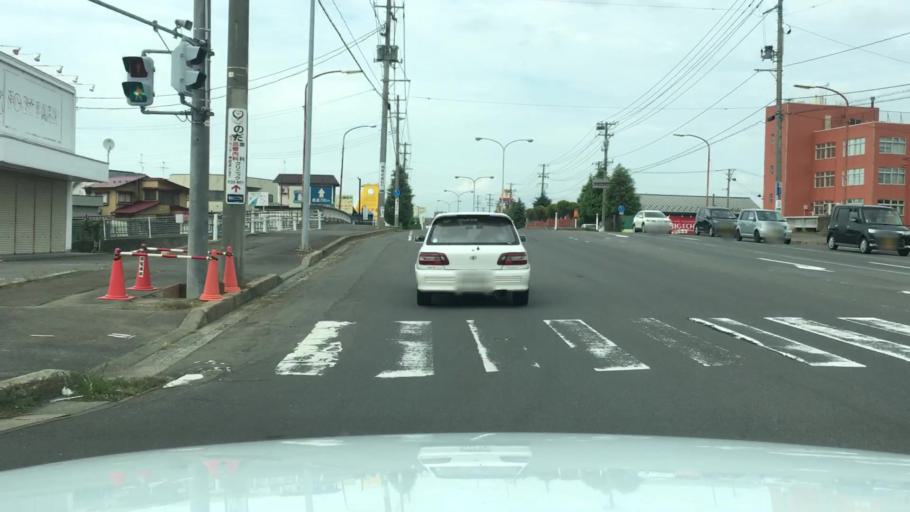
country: JP
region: Aomori
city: Hirosaki
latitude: 40.6101
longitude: 140.4813
